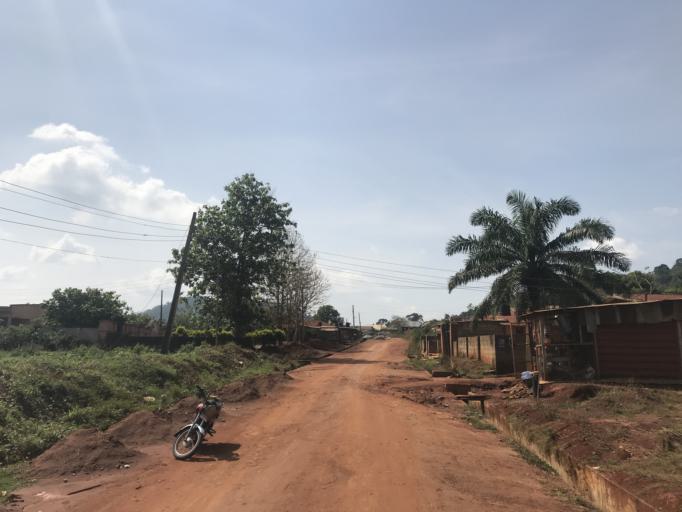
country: NG
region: Osun
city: Ilesa
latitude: 7.6214
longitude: 4.7060
